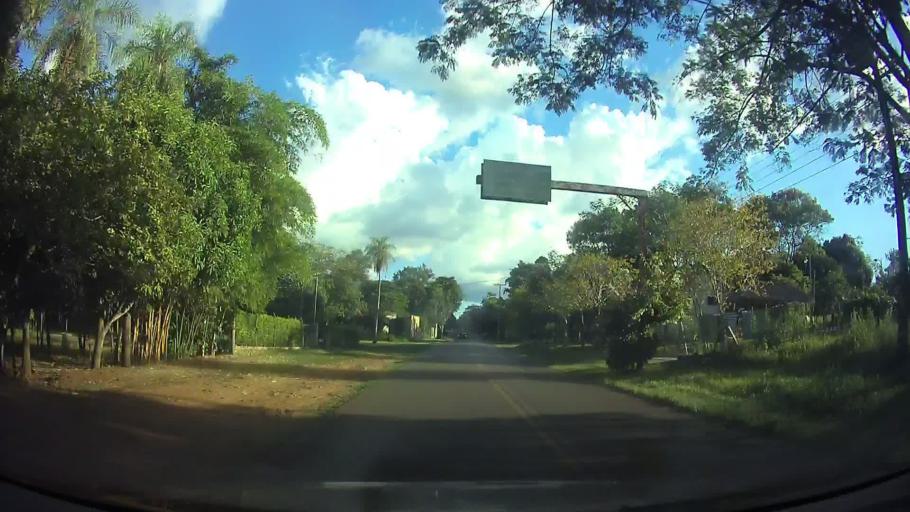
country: PY
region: Cordillera
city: Altos
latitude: -25.1729
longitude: -57.2310
